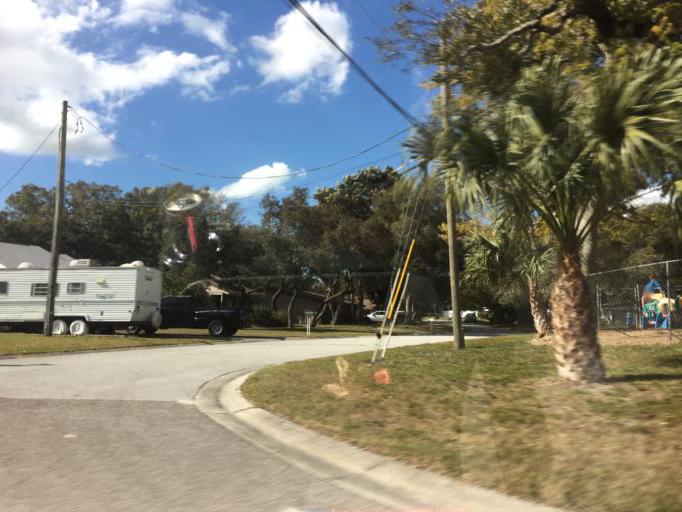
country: US
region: Florida
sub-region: Pinellas County
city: Saint George
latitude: 28.0480
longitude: -82.7429
